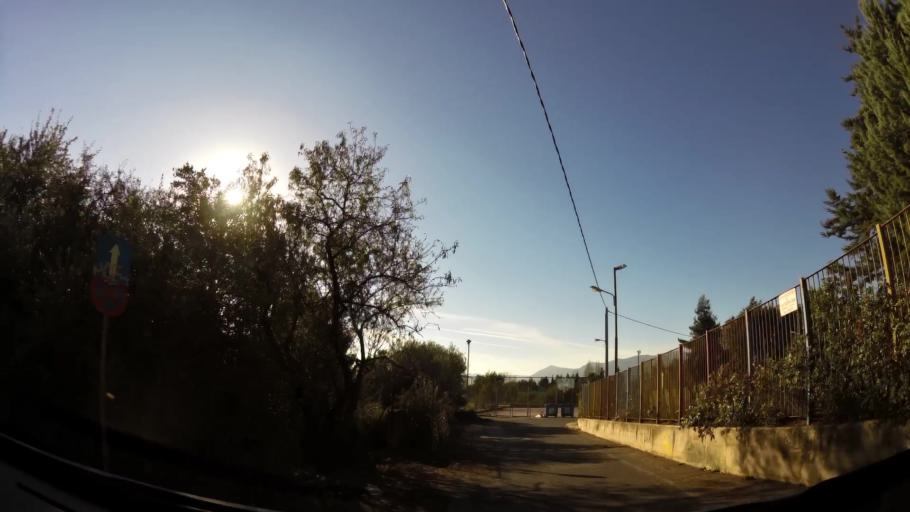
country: GR
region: Attica
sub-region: Nomarchia Anatolikis Attikis
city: Anoixi
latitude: 38.1326
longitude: 23.8552
